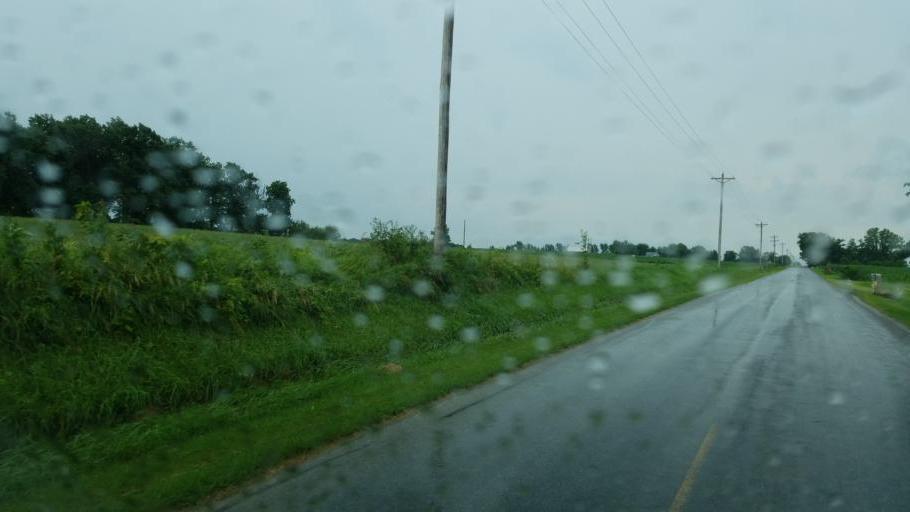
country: US
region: Ohio
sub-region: Union County
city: Richwood
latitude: 40.5395
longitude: -83.4371
